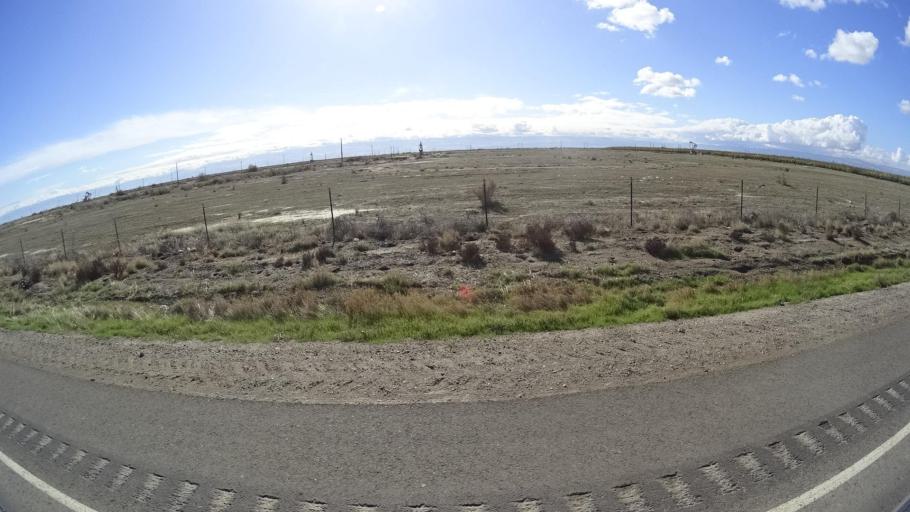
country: US
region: California
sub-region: Kern County
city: Rosedale
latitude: 35.2963
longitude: -119.2363
